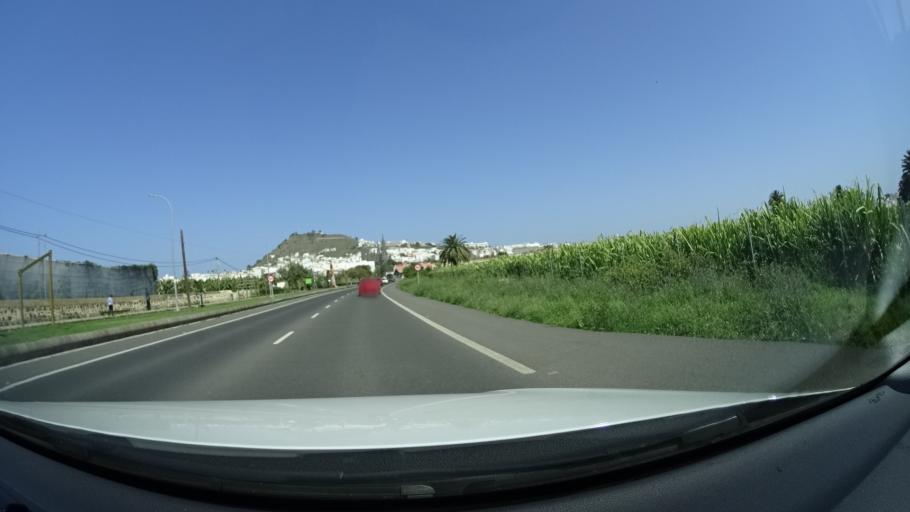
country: ES
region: Canary Islands
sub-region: Provincia de Las Palmas
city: Arucas
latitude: 28.1123
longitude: -15.5256
